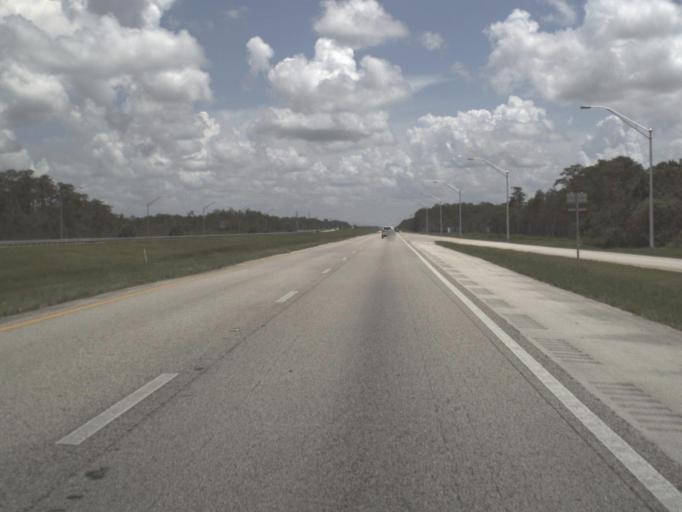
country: US
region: Florida
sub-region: Collier County
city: Immokalee
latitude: 26.1684
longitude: -81.0700
